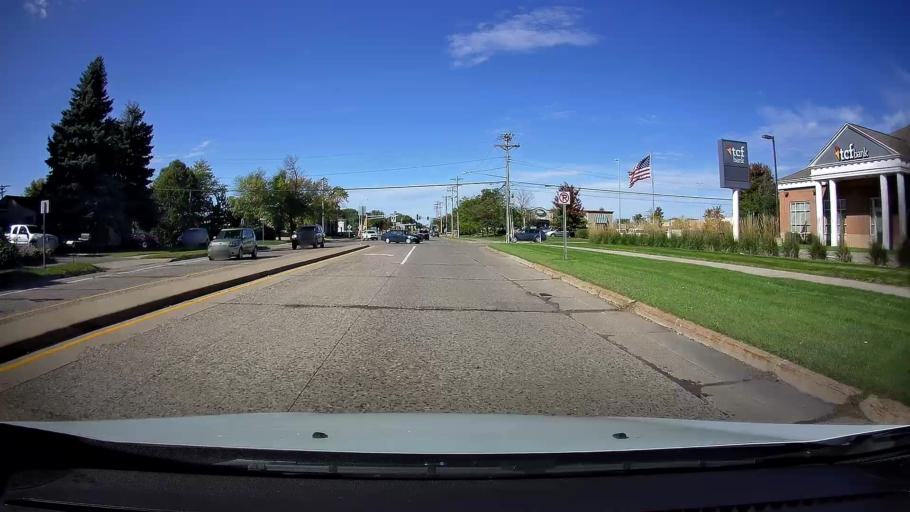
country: US
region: Minnesota
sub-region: Ramsey County
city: Roseville
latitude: 45.0063
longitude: -93.1611
